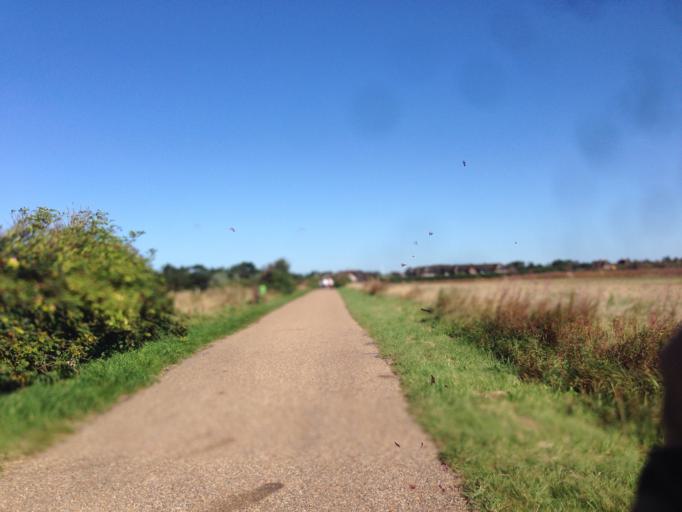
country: DE
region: Schleswig-Holstein
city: Tinnum
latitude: 54.9465
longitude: 8.3349
